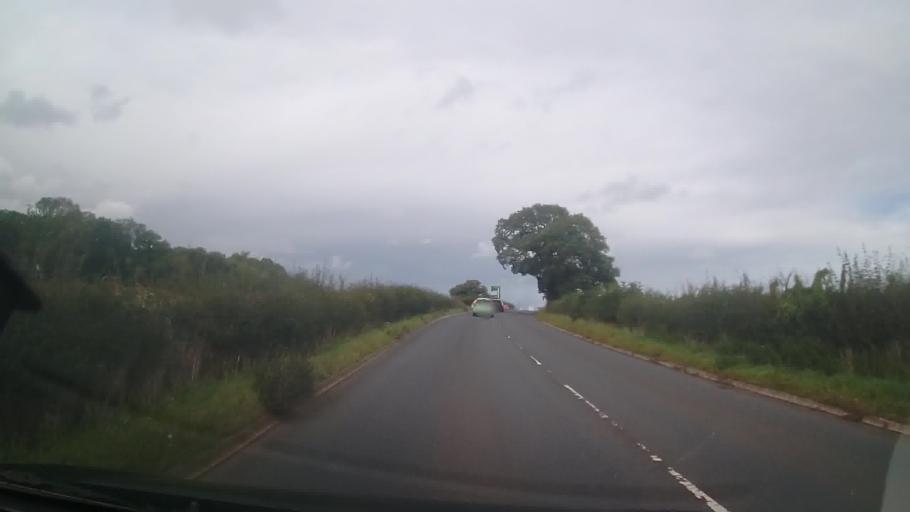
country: GB
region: England
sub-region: Shropshire
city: Alveley
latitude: 52.4770
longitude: -2.3538
